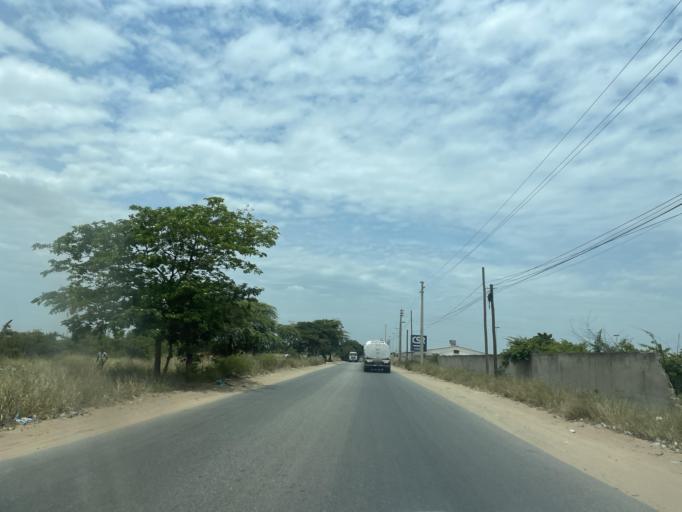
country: AO
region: Luanda
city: Luanda
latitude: -8.9389
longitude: 13.3888
